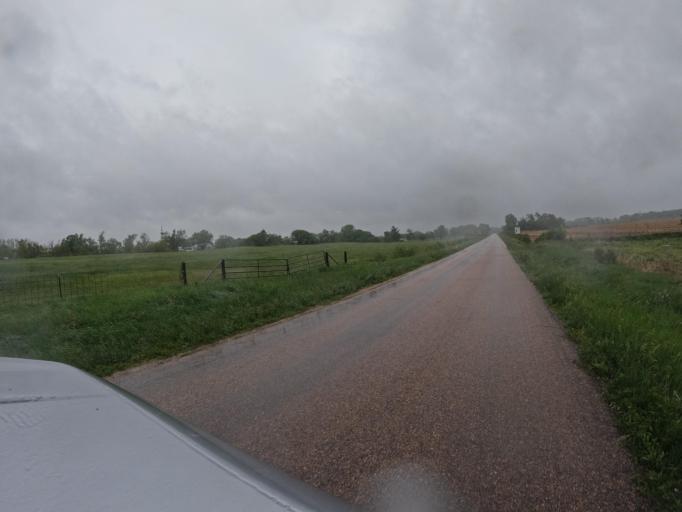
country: US
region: Nebraska
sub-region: Gage County
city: Wymore
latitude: 40.1246
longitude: -96.6527
